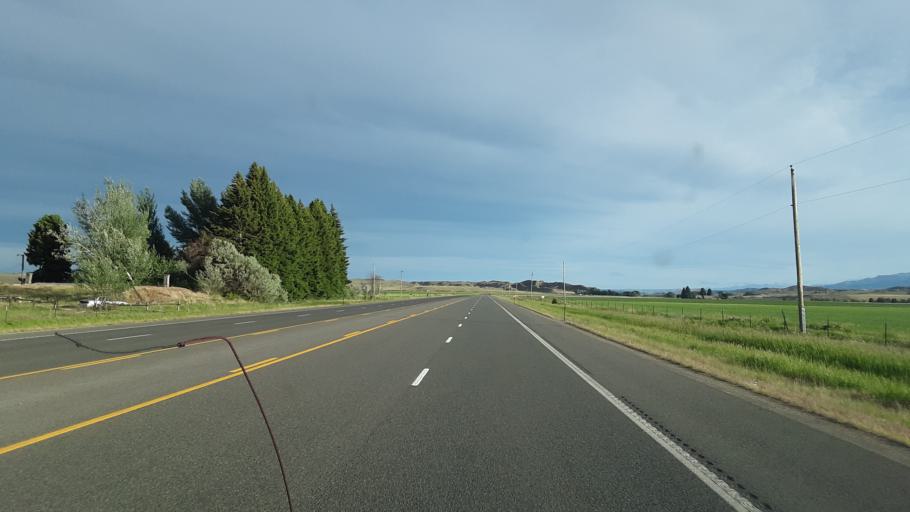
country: US
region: Wyoming
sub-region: Park County
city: Cody
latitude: 44.5619
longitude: -108.9808
